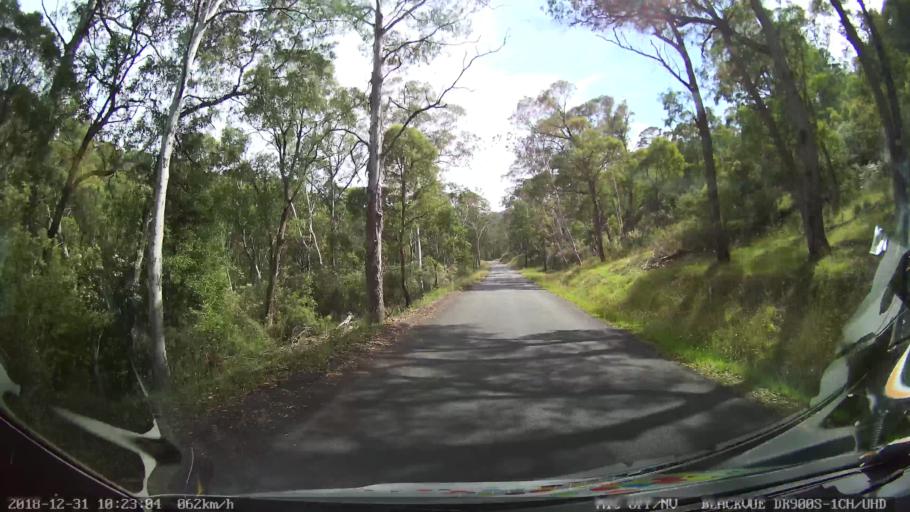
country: AU
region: New South Wales
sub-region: Snowy River
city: Jindabyne
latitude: -36.5200
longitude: 148.1432
